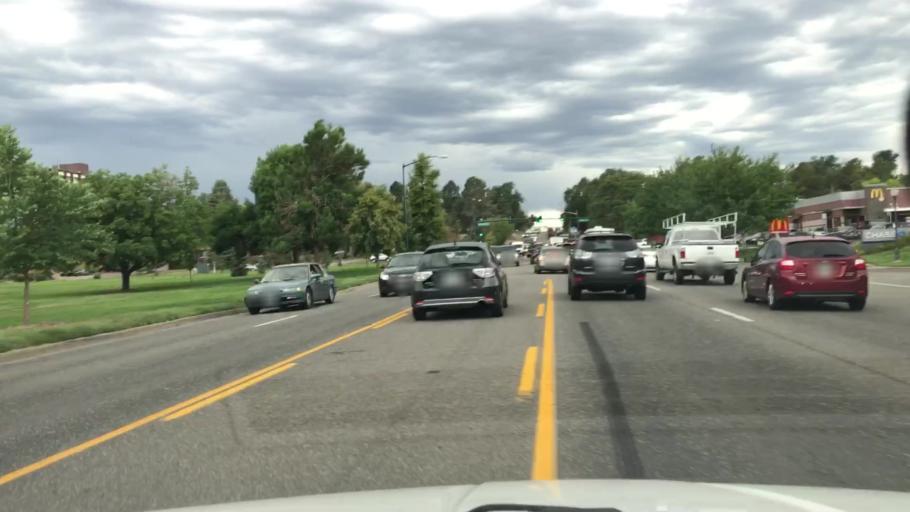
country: US
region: Colorado
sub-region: Jefferson County
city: Edgewater
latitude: 39.7455
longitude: -105.0532
